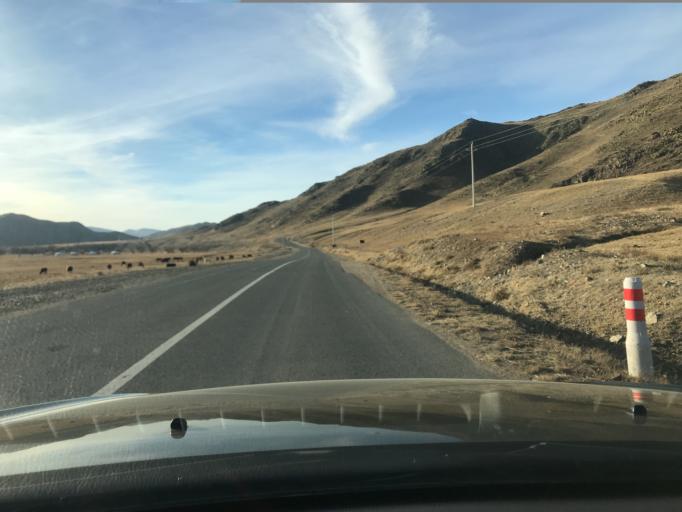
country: MN
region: Central Aimak
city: Dzuunmod
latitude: 47.8229
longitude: 107.3555
